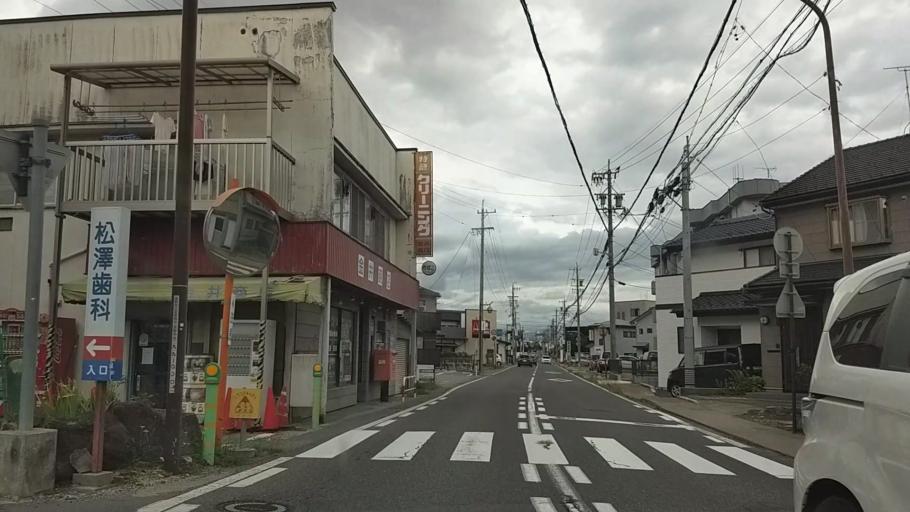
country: JP
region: Nagano
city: Nagano-shi
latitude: 36.6669
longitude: 138.1905
